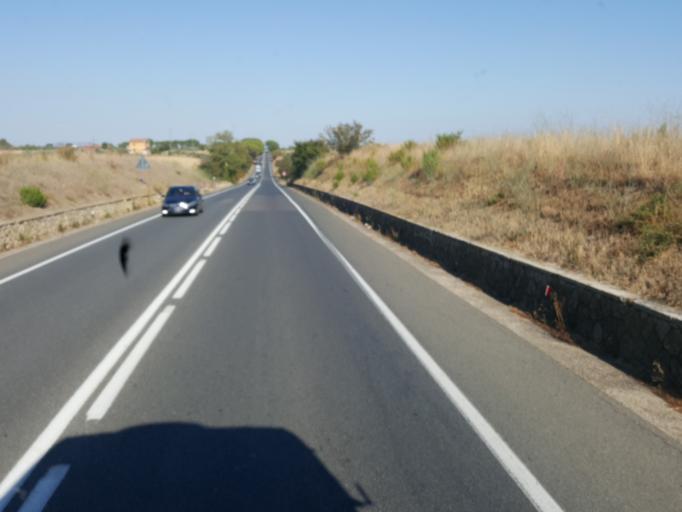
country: IT
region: Tuscany
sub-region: Provincia di Grosseto
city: Capalbio
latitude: 42.4145
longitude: 11.4311
